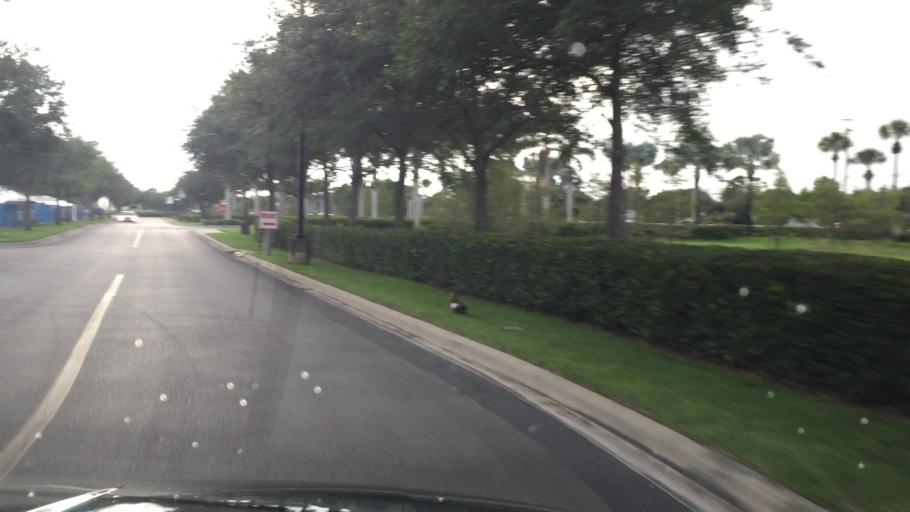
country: US
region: Florida
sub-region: Lee County
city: Villas
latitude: 26.5457
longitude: -81.8487
